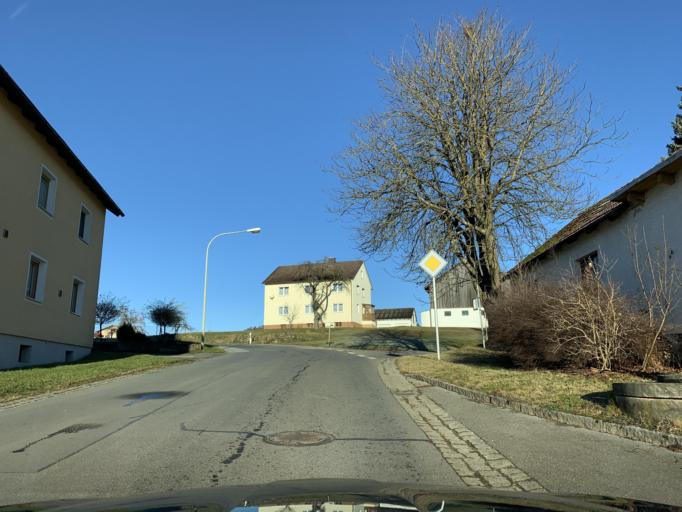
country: DE
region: Bavaria
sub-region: Upper Palatinate
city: Winklarn
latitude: 49.4646
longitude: 12.4667
